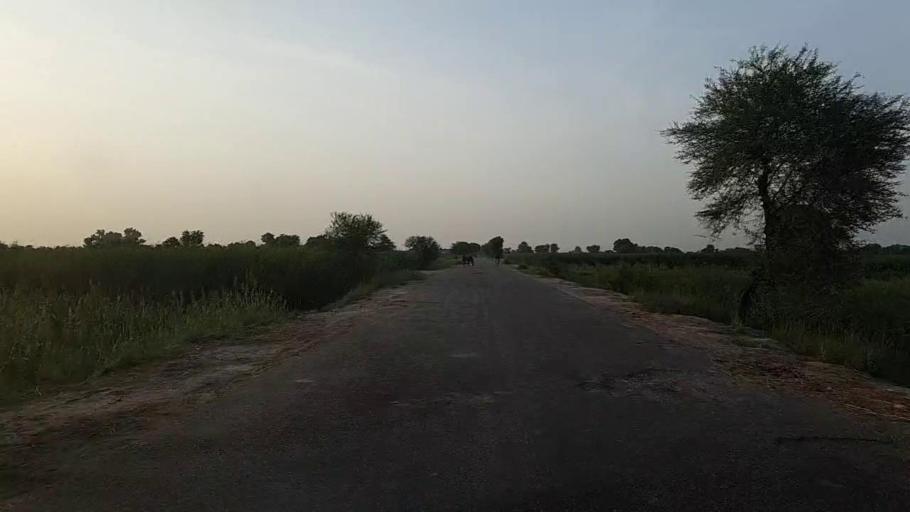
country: PK
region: Sindh
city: Ubauro
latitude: 28.2263
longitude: 69.8180
